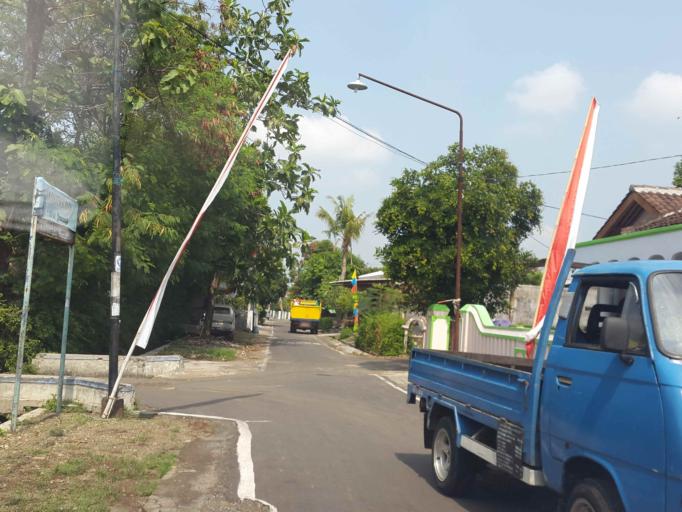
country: ID
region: Central Java
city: Jaten
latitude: -7.5921
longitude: 110.9432
